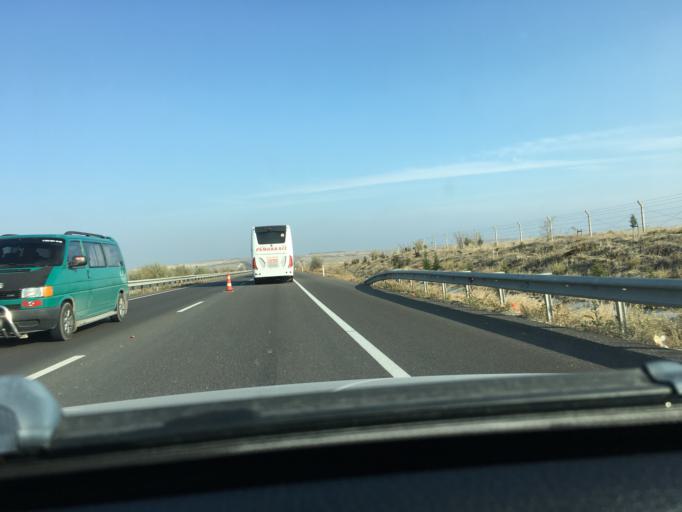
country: TR
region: Eskisehir
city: Gunyuzu
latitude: 39.5746
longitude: 31.8660
